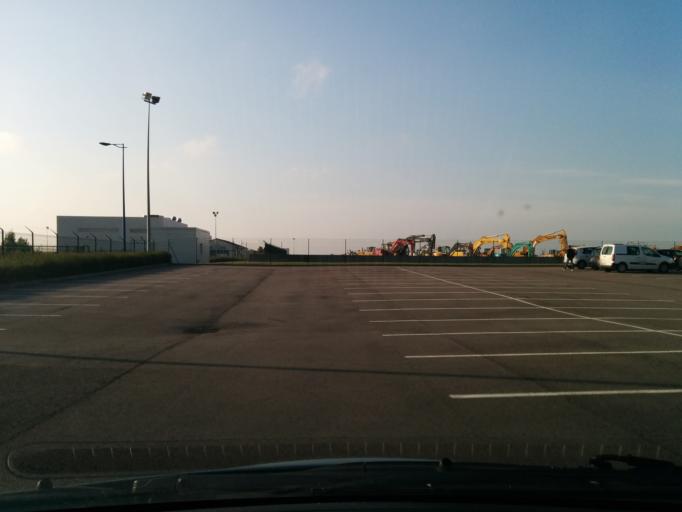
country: FR
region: Haute-Normandie
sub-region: Departement de l'Eure
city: Saint-Aubin-sur-Gaillon
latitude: 49.1369
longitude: 1.3188
